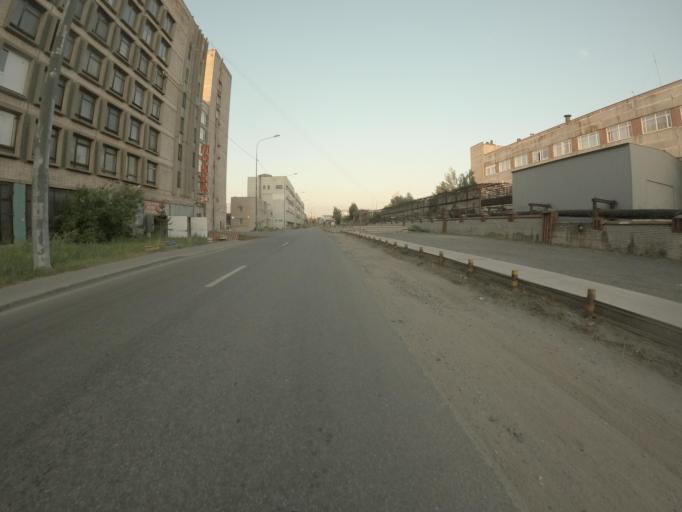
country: RU
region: St.-Petersburg
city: Admiralteisky
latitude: 59.8868
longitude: 30.2868
